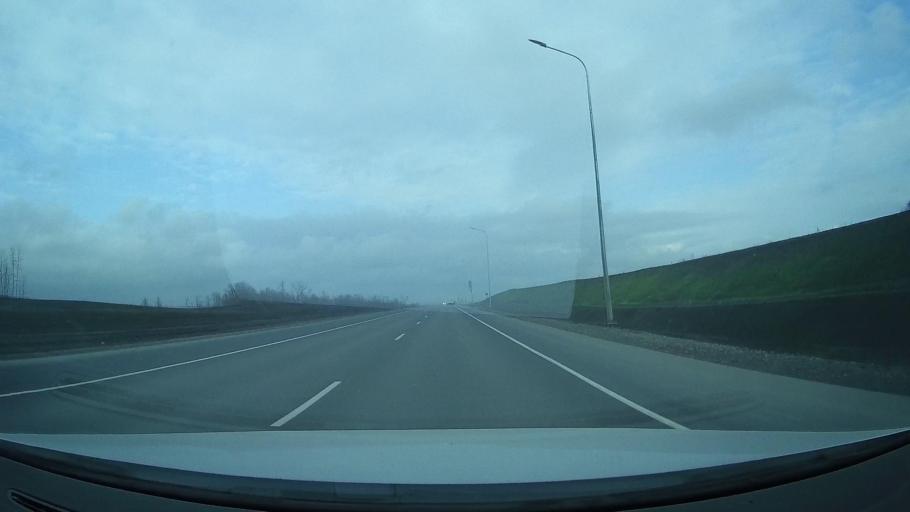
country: RU
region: Rostov
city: Grushevskaya
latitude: 47.4209
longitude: 39.8629
